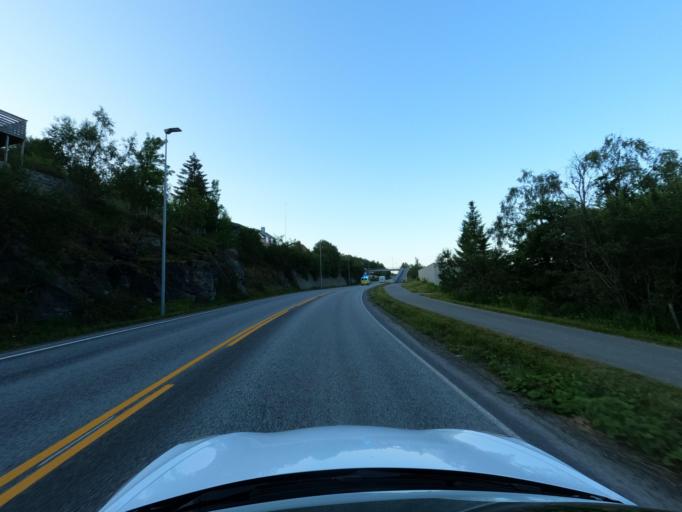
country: NO
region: Troms
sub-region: Harstad
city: Harstad
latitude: 68.7479
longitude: 16.5584
